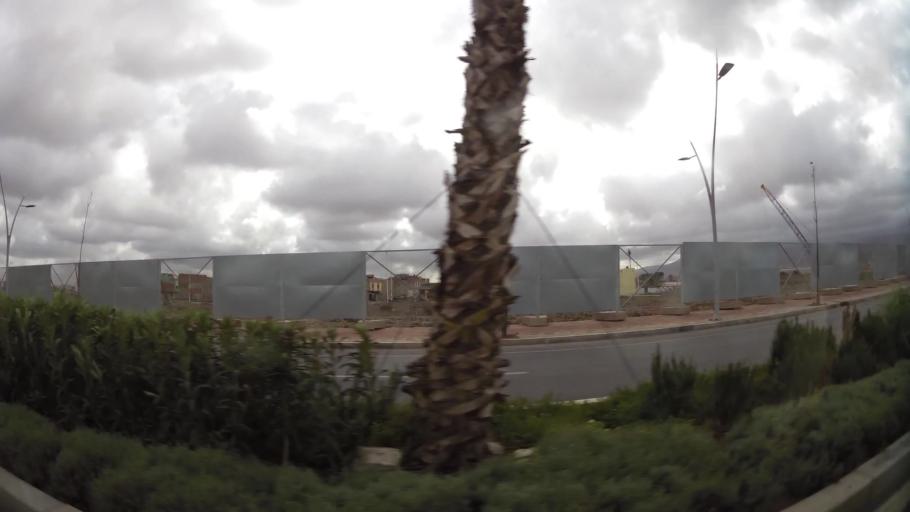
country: MA
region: Oriental
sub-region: Nador
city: Nador
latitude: 35.1603
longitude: -2.9067
